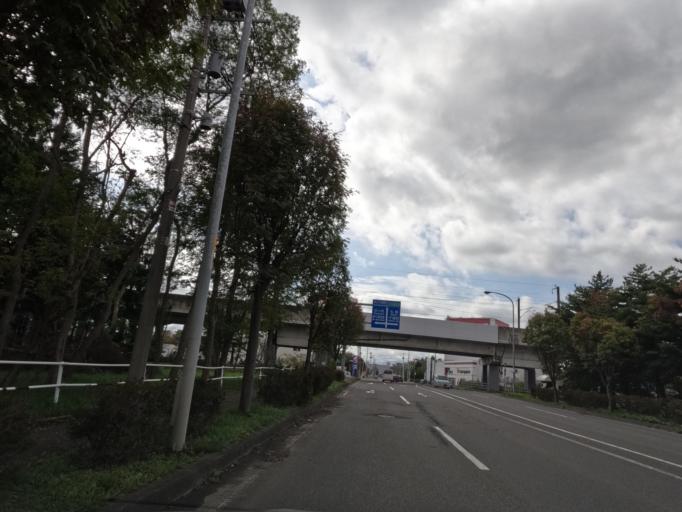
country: JP
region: Hokkaido
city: Chitose
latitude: 42.8221
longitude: 141.6602
